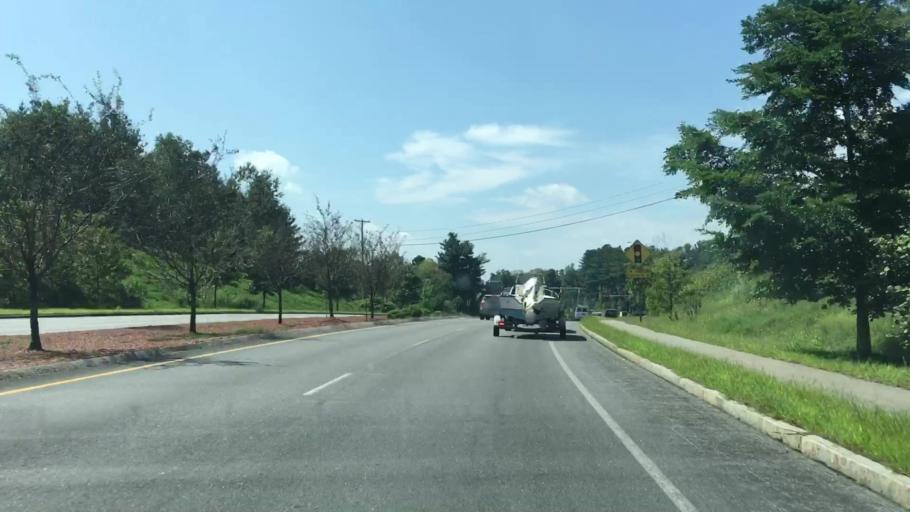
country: US
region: New Hampshire
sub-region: Rockingham County
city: Windham
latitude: 42.8101
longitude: -71.2532
